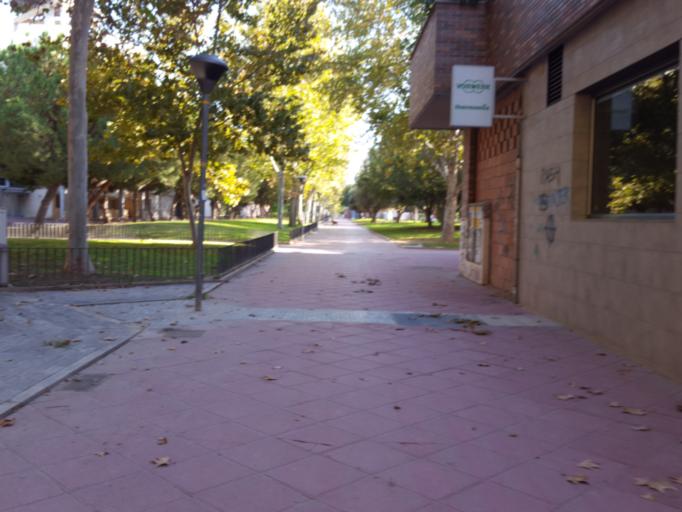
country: ES
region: Murcia
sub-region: Murcia
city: Murcia
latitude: 37.9971
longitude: -1.1252
